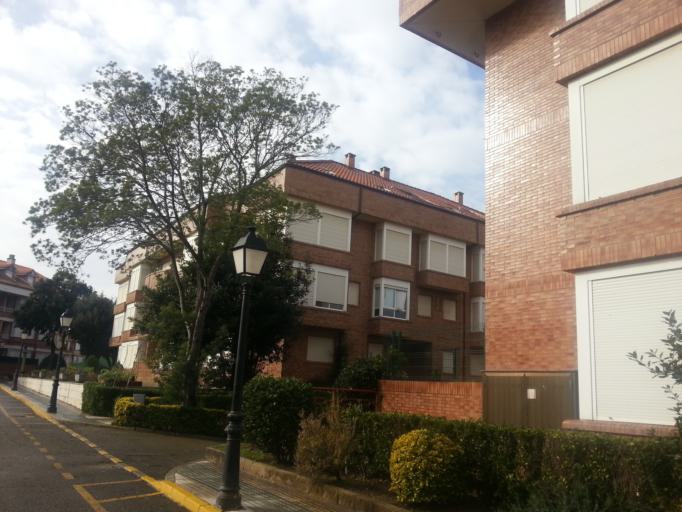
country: ES
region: Cantabria
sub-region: Provincia de Cantabria
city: Noja
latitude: 43.4844
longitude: -3.5220
